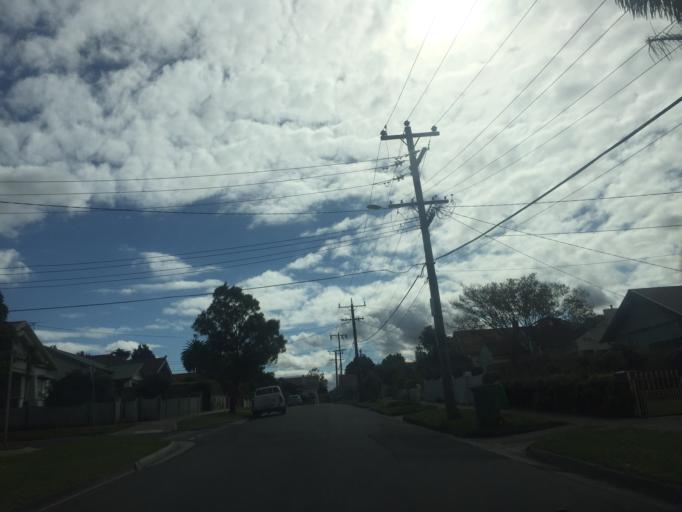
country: AU
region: Victoria
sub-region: Darebin
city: Reservoir
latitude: -37.7290
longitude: 145.0154
